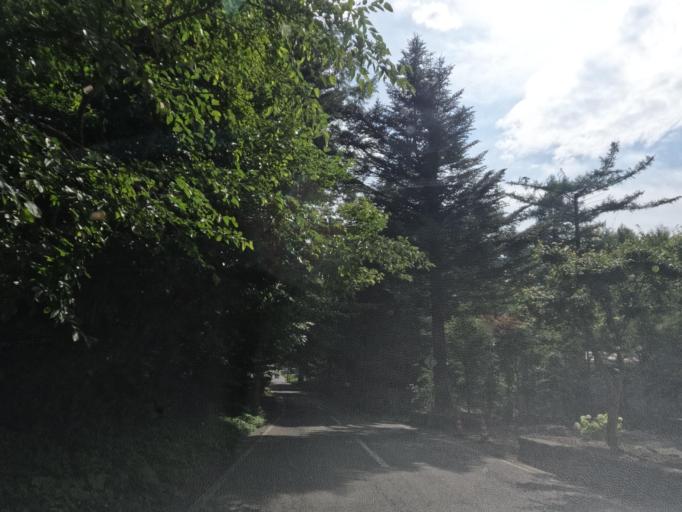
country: JP
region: Nagano
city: Komoro
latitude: 36.3531
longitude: 138.6018
